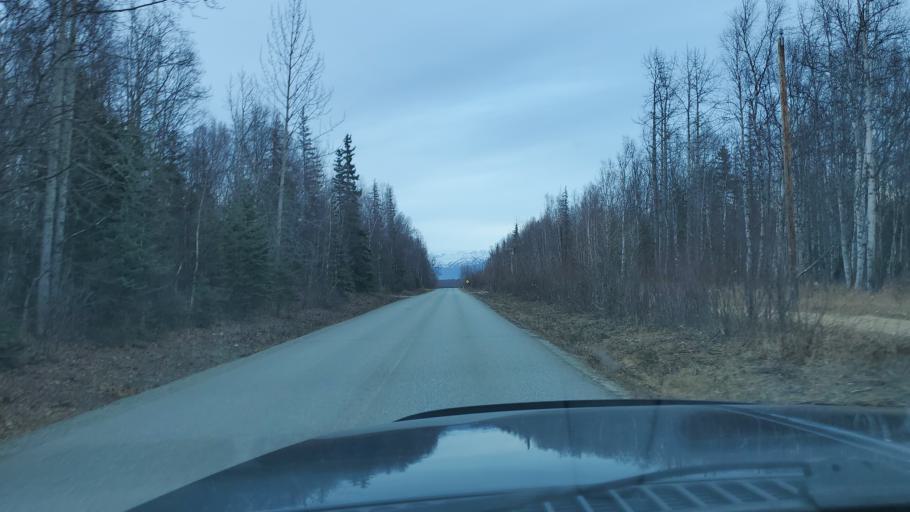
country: US
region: Alaska
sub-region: Matanuska-Susitna Borough
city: Lakes
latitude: 61.6572
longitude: -149.3011
